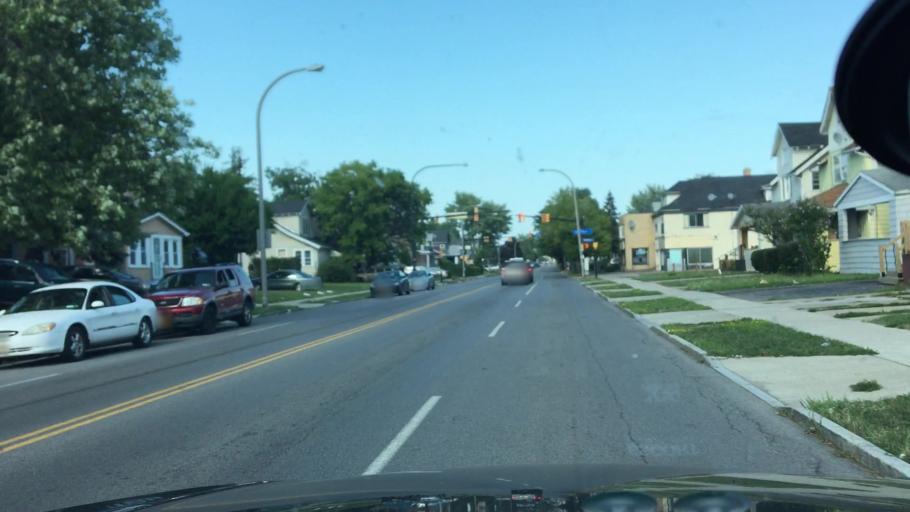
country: US
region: New York
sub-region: Erie County
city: Eggertsville
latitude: 42.9387
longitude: -78.8117
